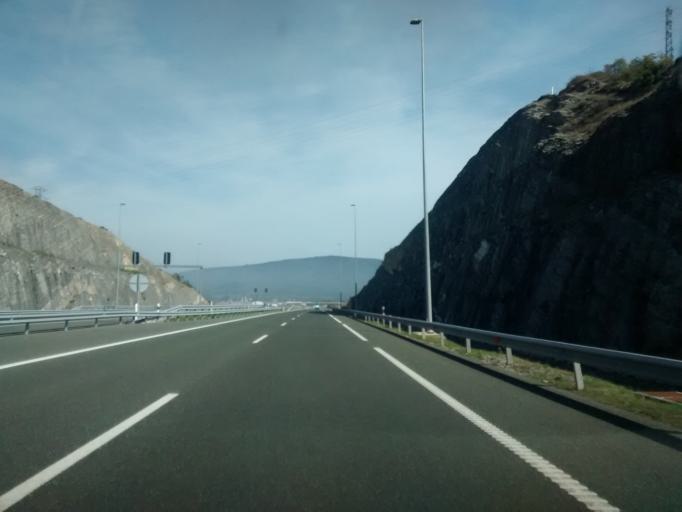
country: ES
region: Basque Country
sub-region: Provincia de Guipuzcoa
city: Leintz-Gatzaga
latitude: 42.9426
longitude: -2.6301
